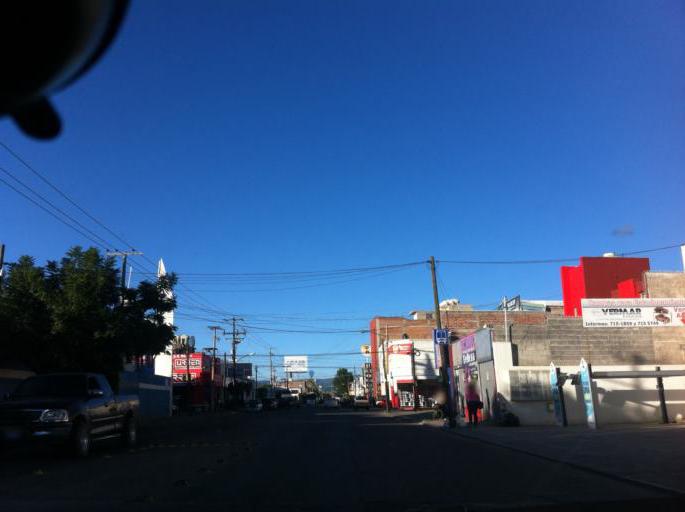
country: MX
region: Guanajuato
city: Leon
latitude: 21.1054
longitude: -101.6905
